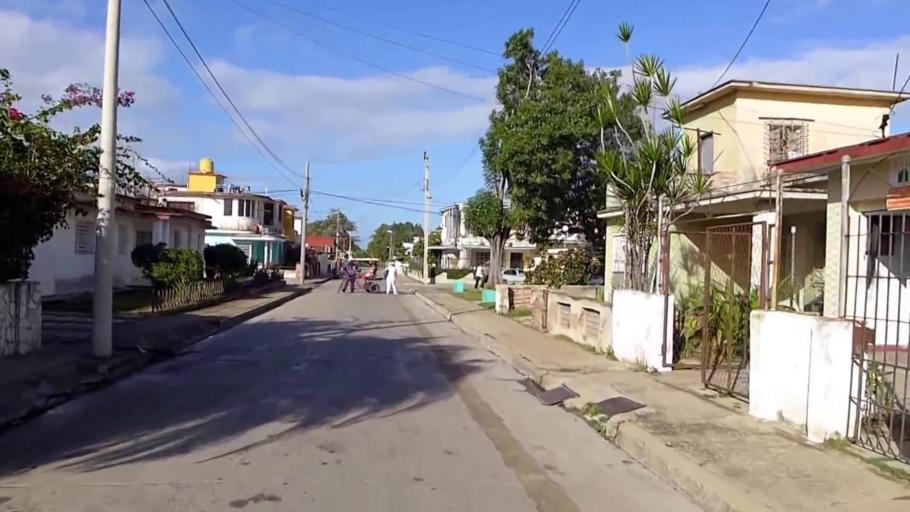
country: CU
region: Camaguey
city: Camaguey
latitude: 21.3865
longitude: -77.9229
